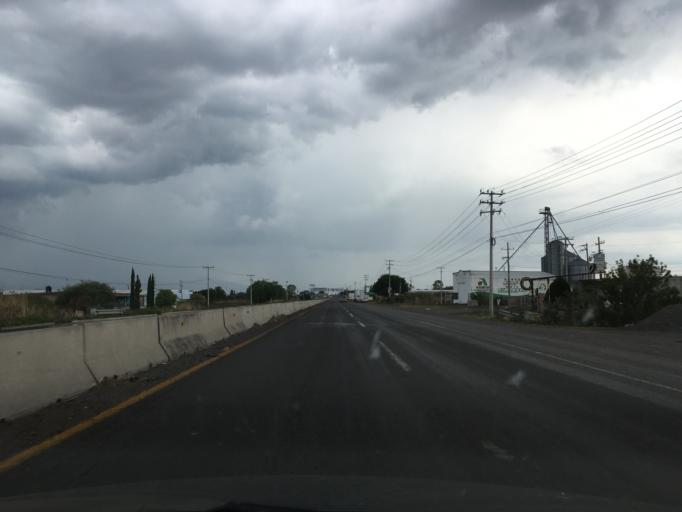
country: MX
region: Guanajuato
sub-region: Celaya
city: El Sauz (El Sauz de Villasenor)
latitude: 20.3825
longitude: -100.7936
